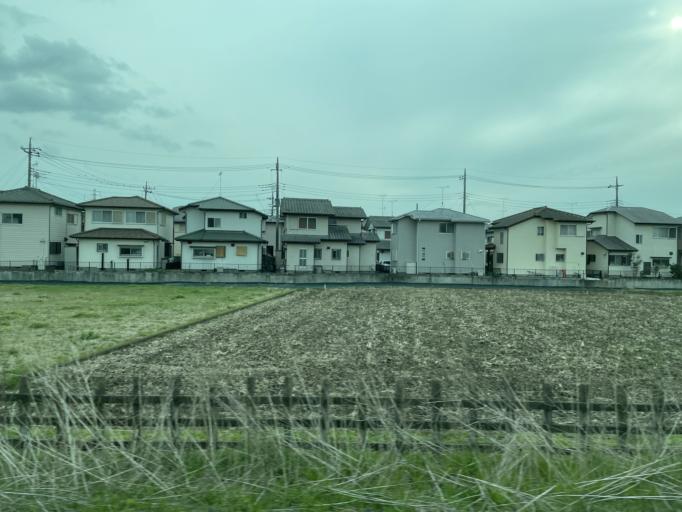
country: JP
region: Saitama
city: Kukichuo
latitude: 36.0536
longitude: 139.6826
